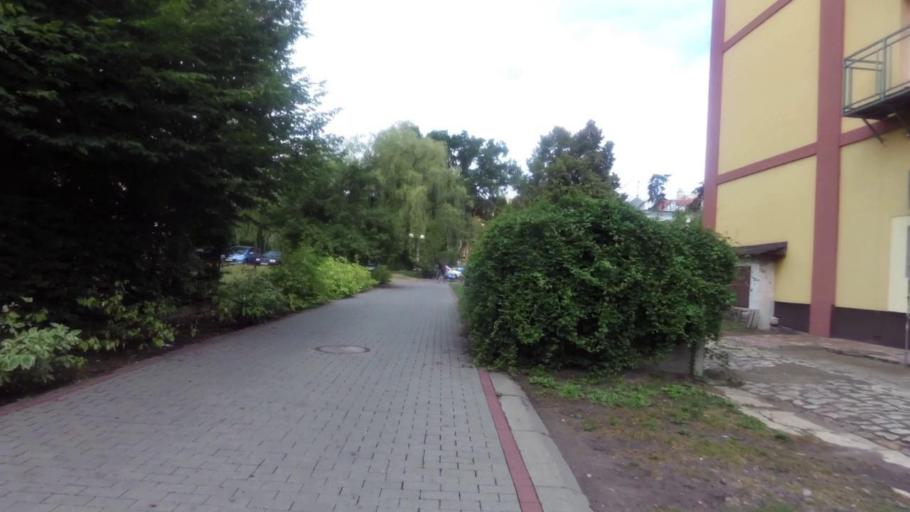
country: PL
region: West Pomeranian Voivodeship
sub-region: Powiat mysliborski
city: Debno
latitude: 52.7388
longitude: 14.7031
